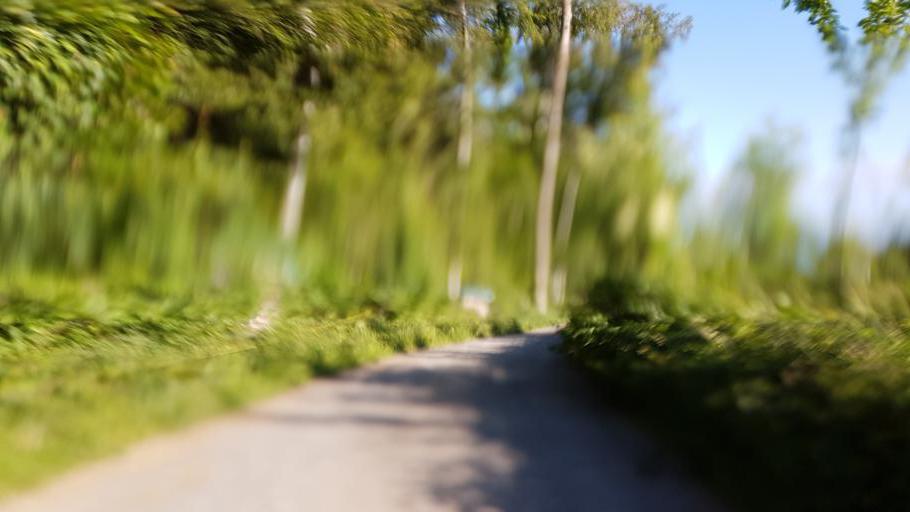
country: CH
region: Bern
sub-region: Bern-Mittelland District
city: Rubigen
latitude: 46.8905
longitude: 7.5590
